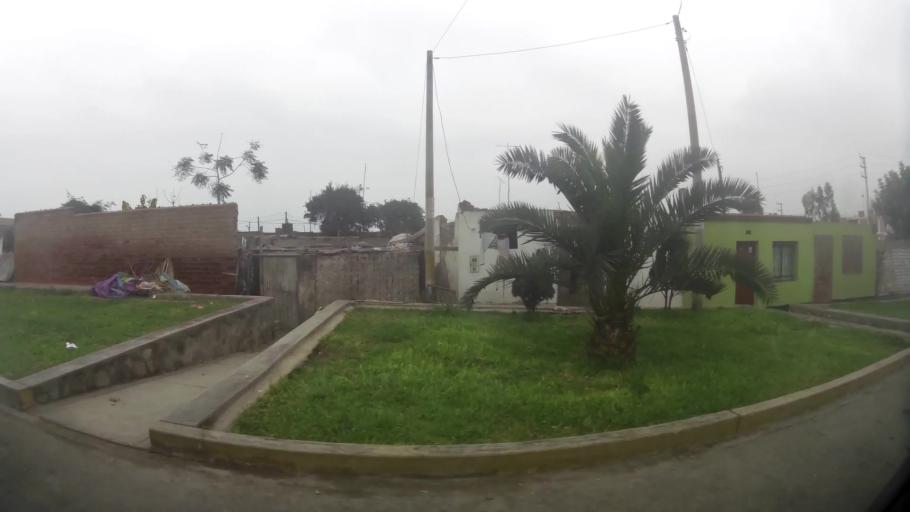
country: PE
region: Lima
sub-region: Provincia de Huaral
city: Chancay
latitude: -11.5862
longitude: -77.2719
